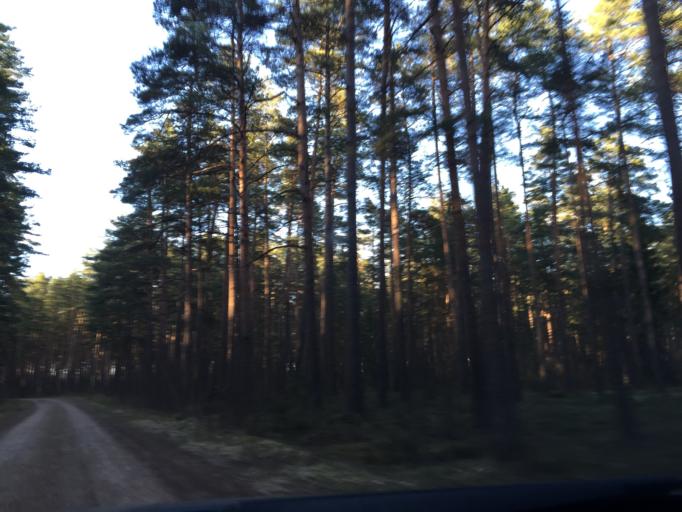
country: LV
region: Kekava
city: Kekava
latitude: 56.8664
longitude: 24.2214
